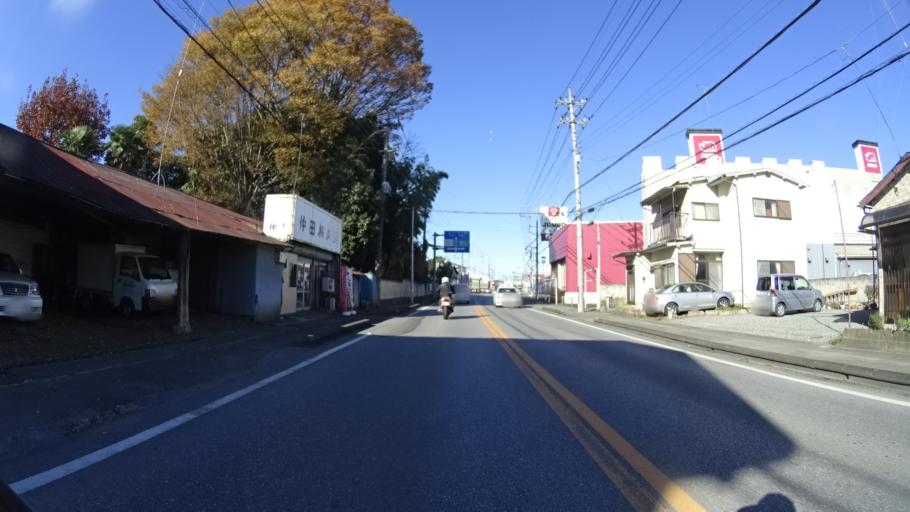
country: JP
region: Tochigi
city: Kanuma
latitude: 36.5498
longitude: 139.7473
